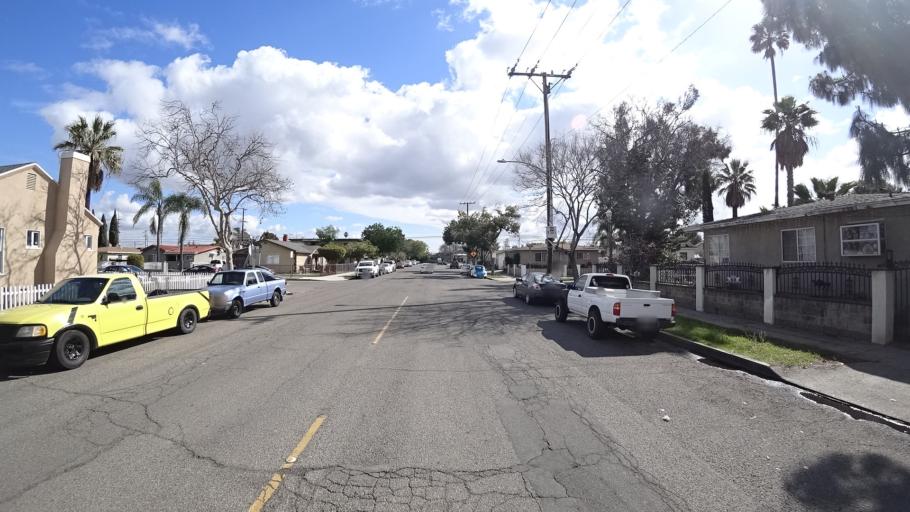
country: US
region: California
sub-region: Orange County
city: Anaheim
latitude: 33.8455
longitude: -117.9115
